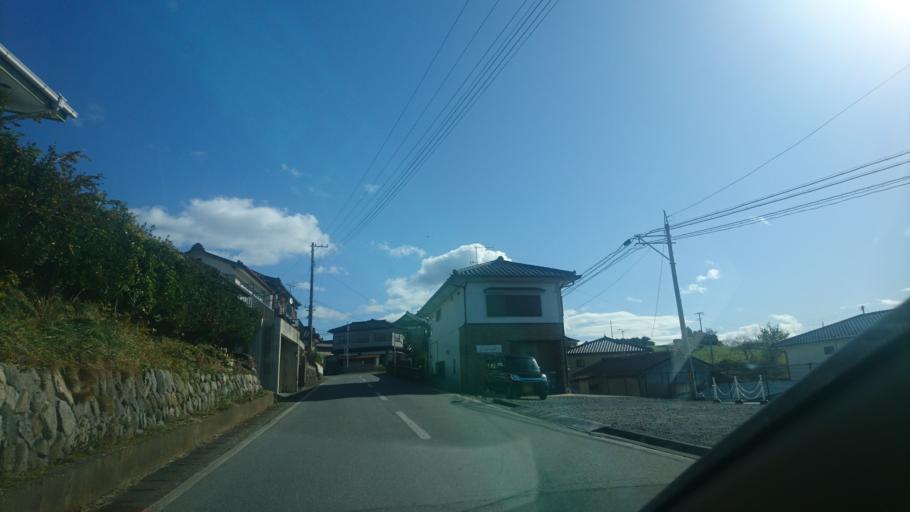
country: JP
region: Iwate
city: Ofunato
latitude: 38.9906
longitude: 141.7328
